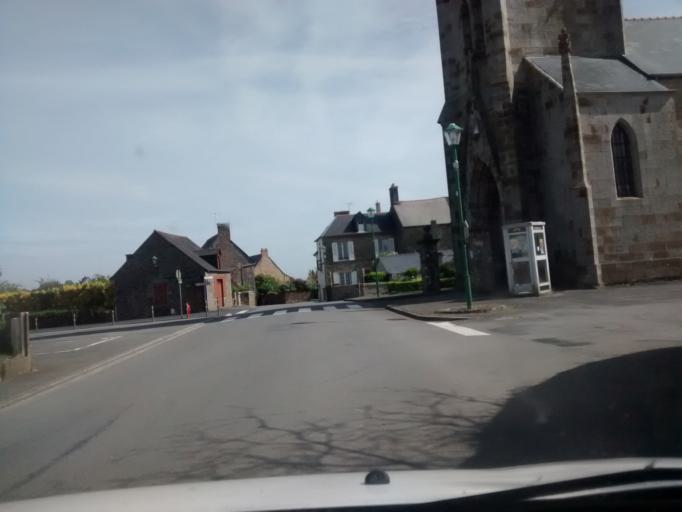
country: FR
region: Brittany
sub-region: Departement d'Ille-et-Vilaine
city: Antrain
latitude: 48.4675
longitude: -1.5034
